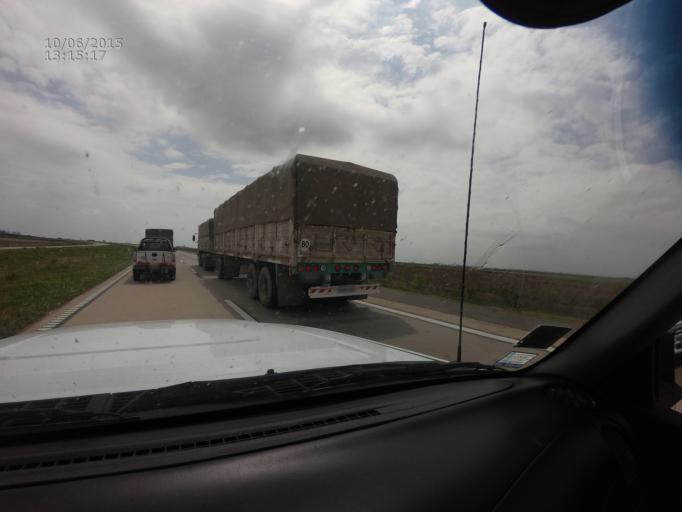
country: AR
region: Cordoba
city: General Roca
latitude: -32.6985
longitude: -61.9515
